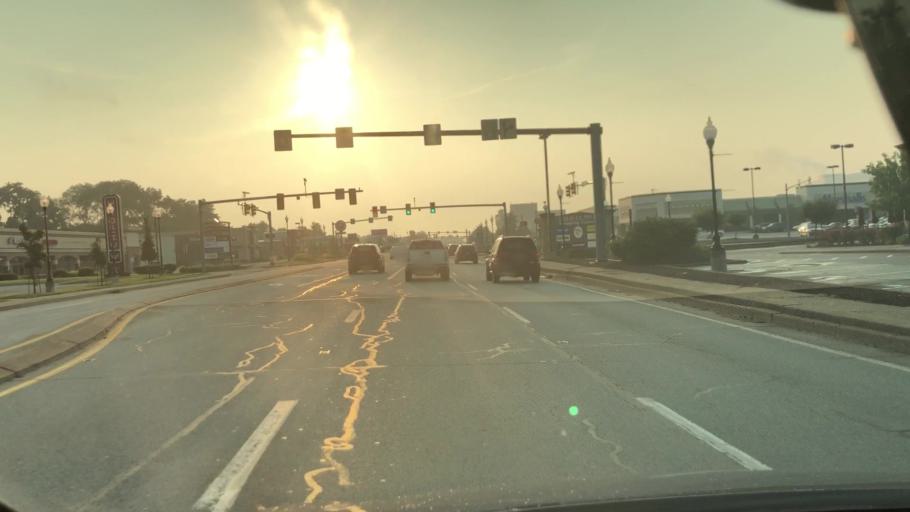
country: US
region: Pennsylvania
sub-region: Allegheny County
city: Monroeville
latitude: 40.4388
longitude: -79.7672
